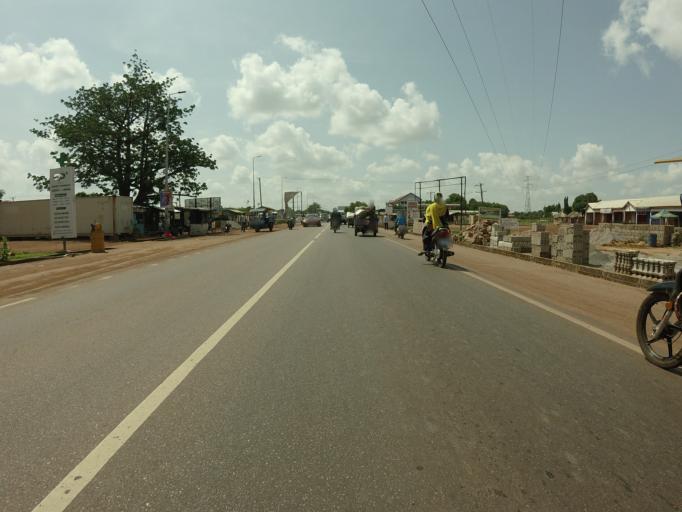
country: GH
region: Northern
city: Tamale
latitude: 9.4495
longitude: -0.8448
